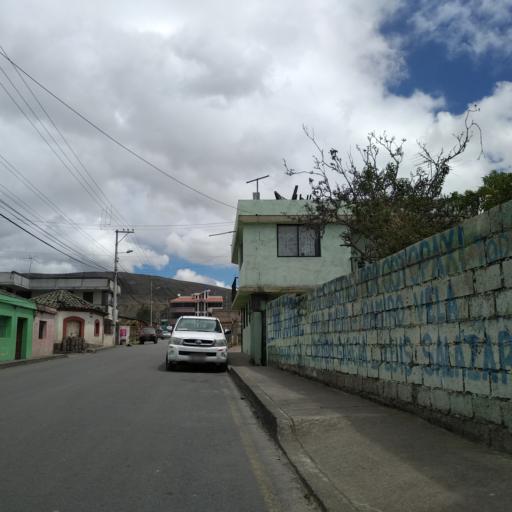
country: EC
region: Cotopaxi
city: Saquisili
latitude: -0.7568
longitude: -78.6851
